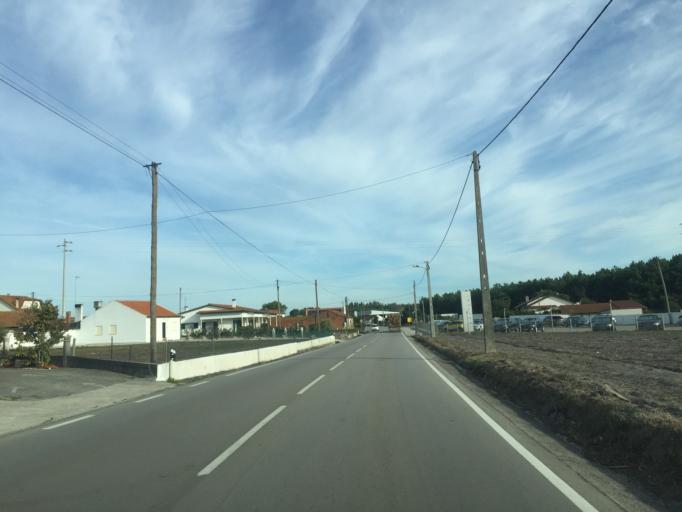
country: PT
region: Leiria
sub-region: Pombal
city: Lourical
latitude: 39.9959
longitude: -8.8040
